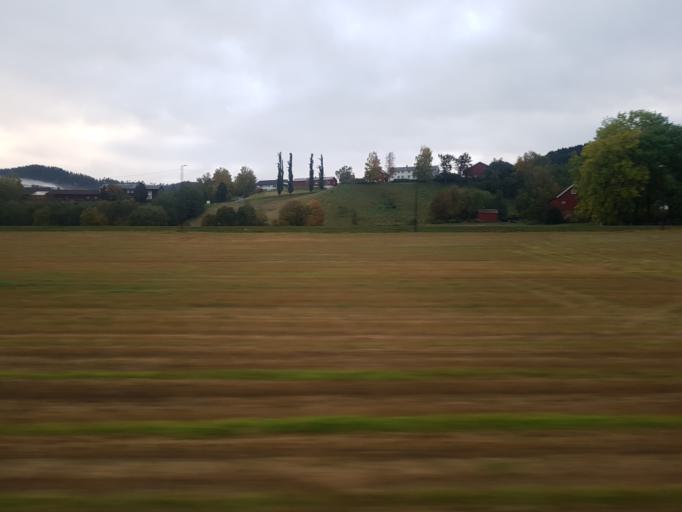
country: NO
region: Sor-Trondelag
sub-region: Melhus
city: Lundamo
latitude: 63.1336
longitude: 10.2551
